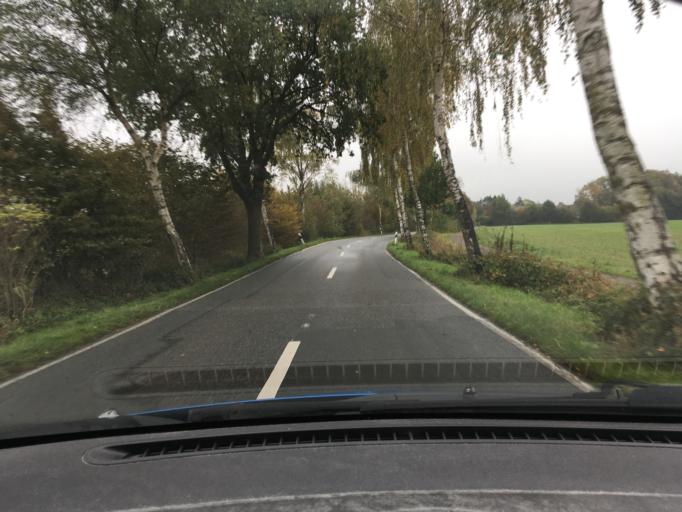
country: DE
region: Schleswig-Holstein
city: Bosau
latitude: 54.0927
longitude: 10.4696
